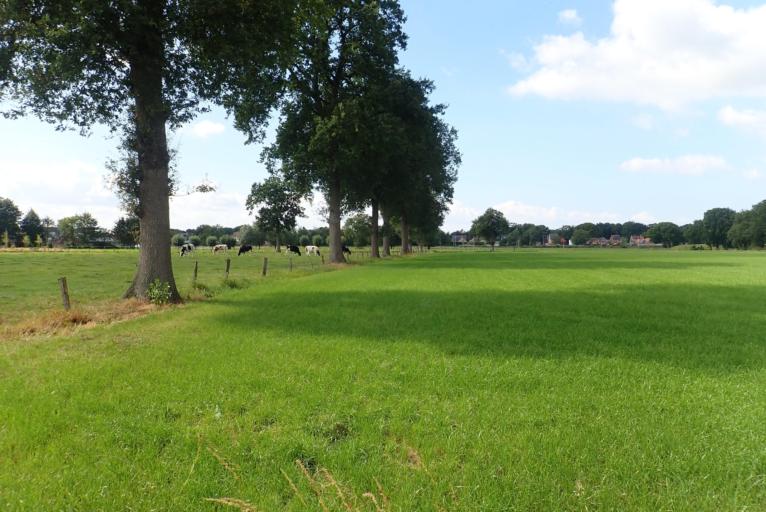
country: BE
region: Flanders
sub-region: Provincie Antwerpen
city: Essen
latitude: 51.4303
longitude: 4.4684
